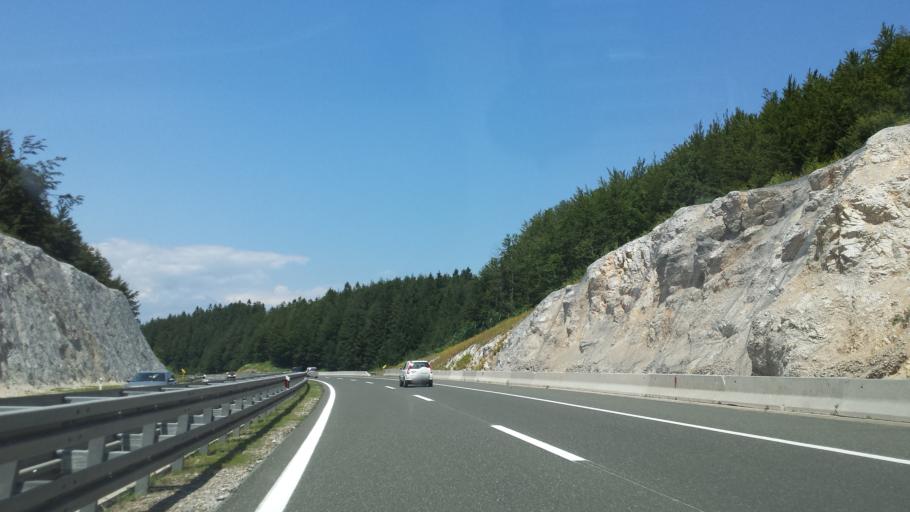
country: HR
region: Primorsko-Goranska
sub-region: Grad Delnice
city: Delnice
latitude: 45.3905
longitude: 14.8323
